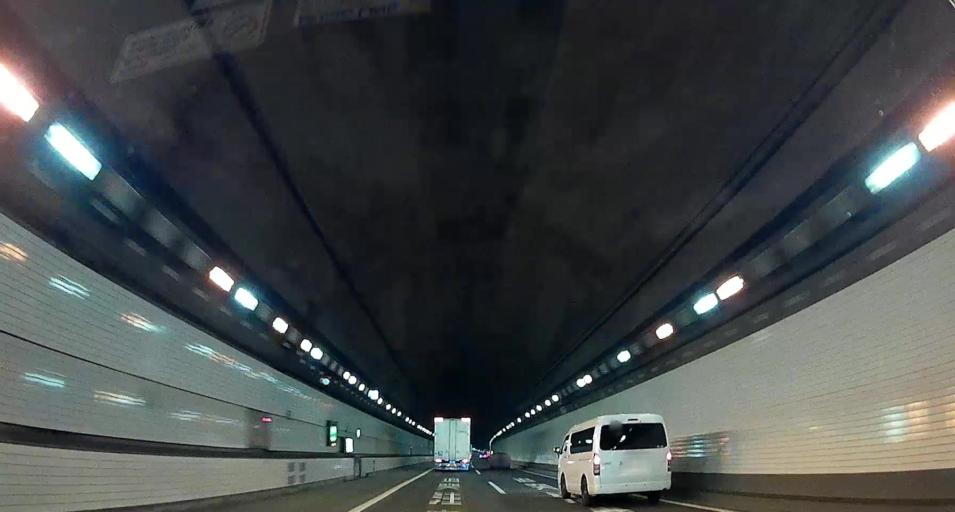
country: JP
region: Chiba
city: Kisarazu
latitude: 35.4644
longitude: 139.8740
